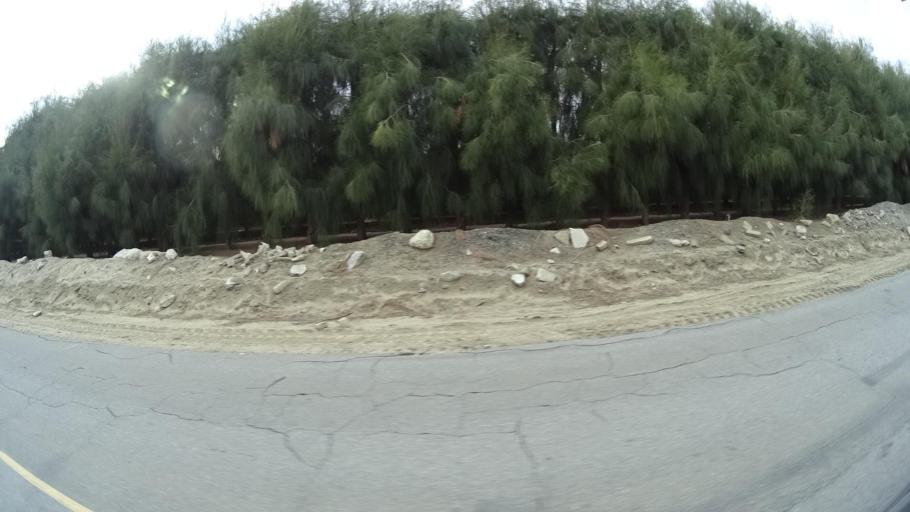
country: US
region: California
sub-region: Kern County
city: Arvin
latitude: 35.1563
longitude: -118.8236
